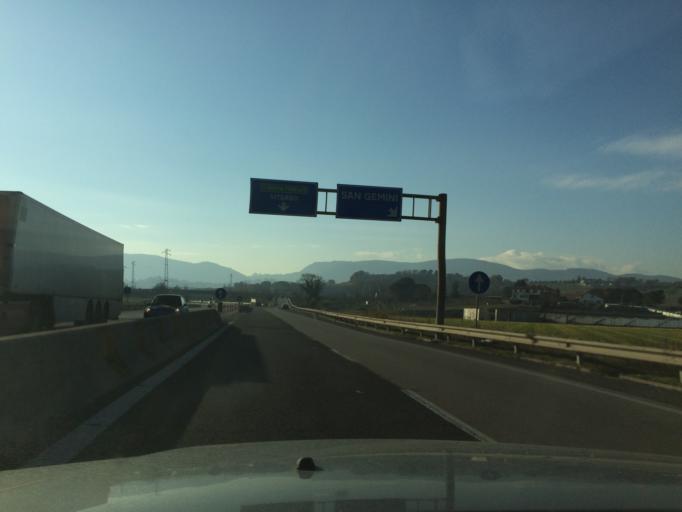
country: IT
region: Umbria
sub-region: Provincia di Terni
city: Narni Scalo
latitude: 42.5599
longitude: 12.5412
